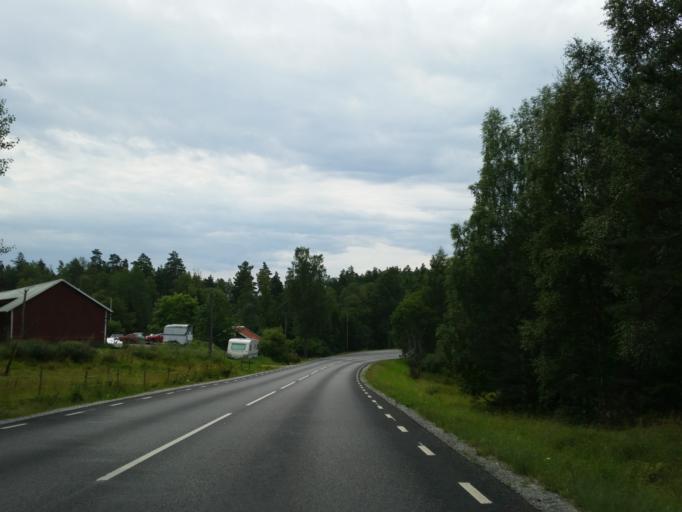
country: SE
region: Stockholm
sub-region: Sodertalje Kommun
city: Soedertaelje
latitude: 59.2177
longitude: 17.6665
